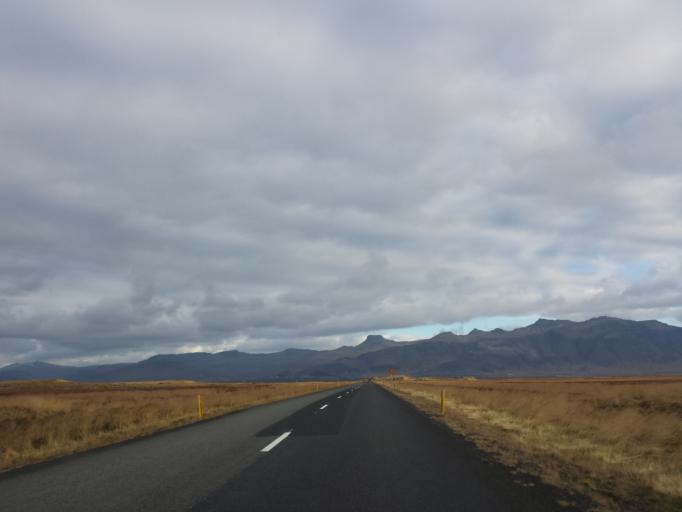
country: IS
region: West
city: Stykkisholmur
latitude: 64.8465
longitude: -22.3629
